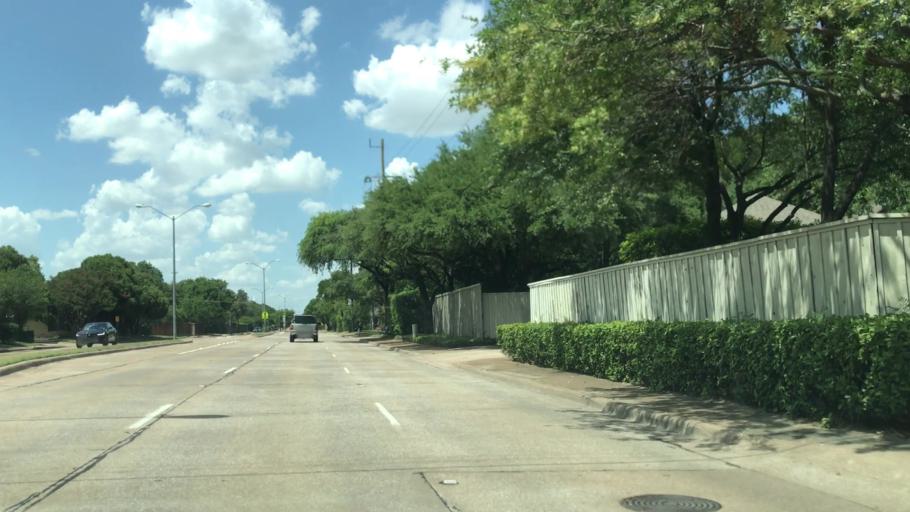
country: US
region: Texas
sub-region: Dallas County
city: University Park
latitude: 32.8748
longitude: -96.8384
